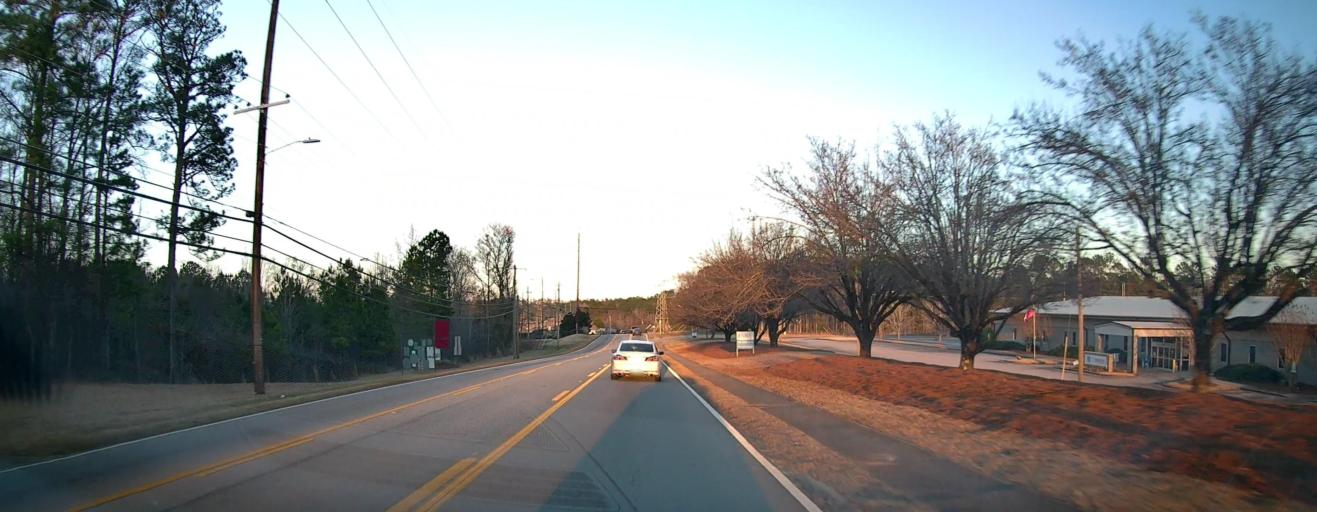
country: US
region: Georgia
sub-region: Troup County
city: La Grange
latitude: 33.0529
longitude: -85.0032
